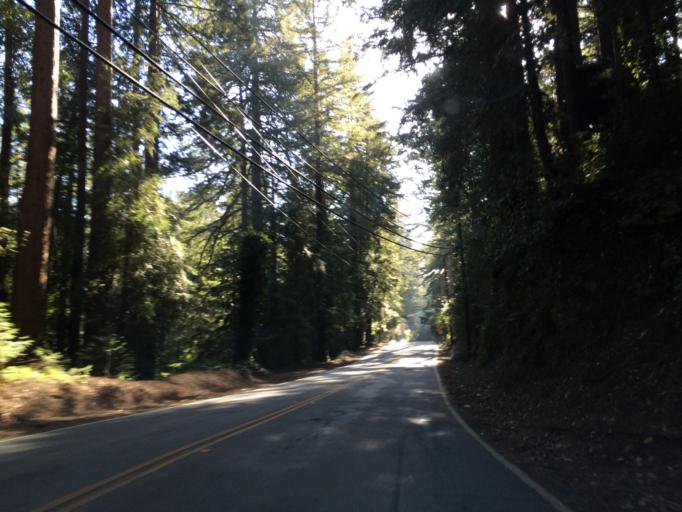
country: US
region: California
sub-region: Santa Cruz County
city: Boulder Creek
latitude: 37.1399
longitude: -122.1507
